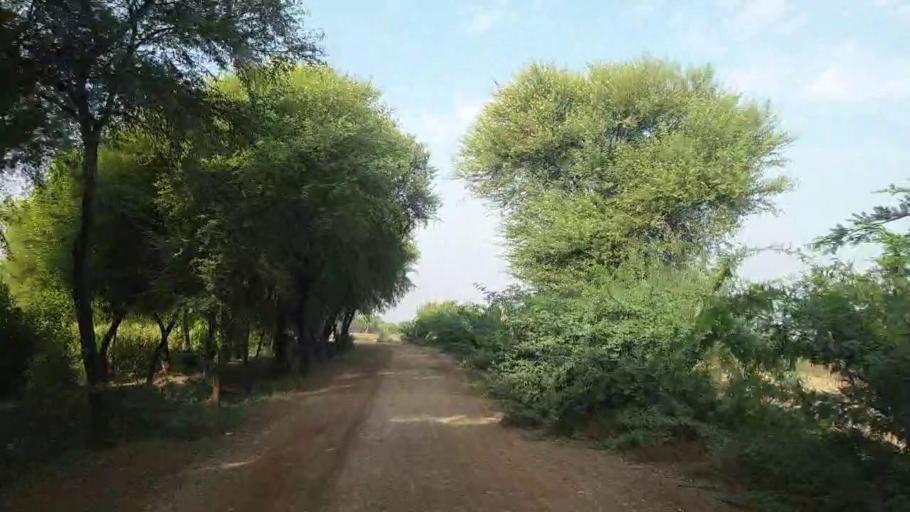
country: PK
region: Sindh
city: Tando Bago
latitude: 24.8552
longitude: 68.9912
